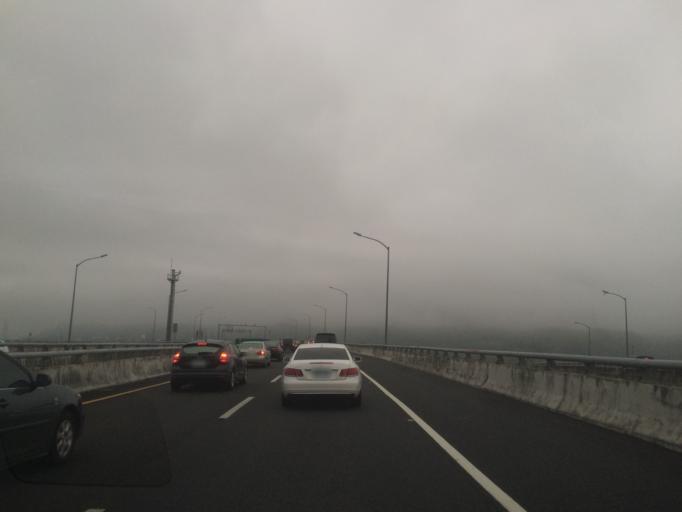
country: TW
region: Taiwan
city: Zhongxing New Village
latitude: 24.0051
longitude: 120.8152
